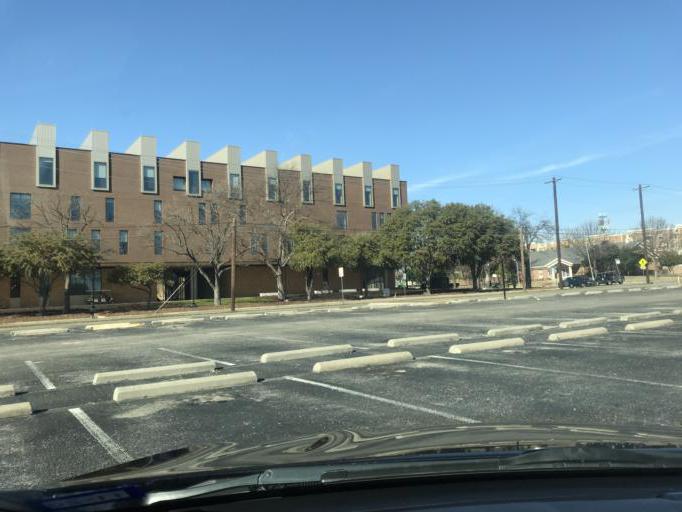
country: US
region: Texas
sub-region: Denton County
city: Denton
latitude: 33.2128
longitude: -97.1438
